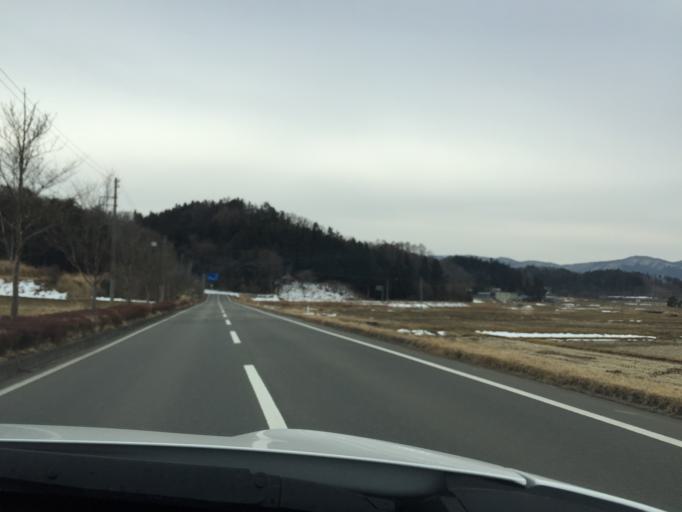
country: JP
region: Fukushima
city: Funehikimachi-funehiki
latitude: 37.4004
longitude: 140.6160
